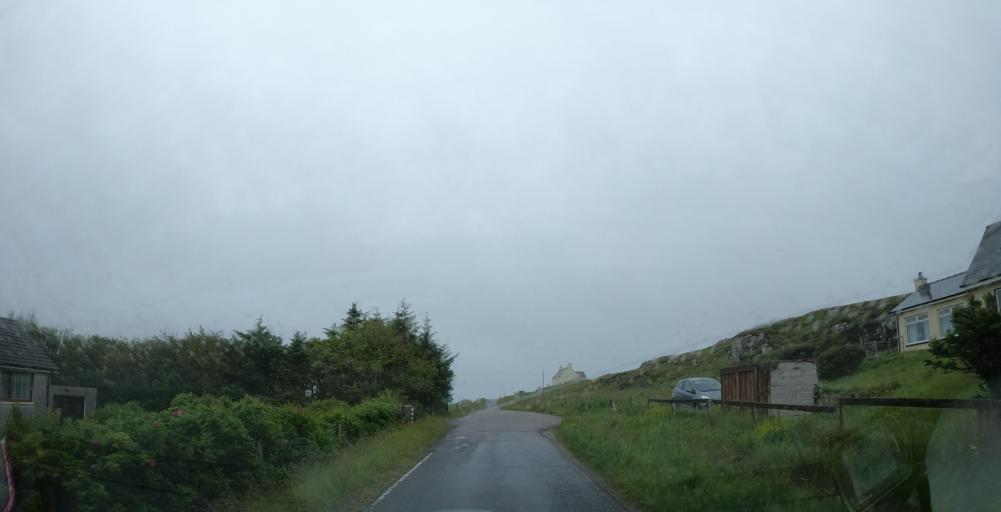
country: GB
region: Scotland
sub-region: Eilean Siar
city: Barra
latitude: 56.9882
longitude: -7.4146
